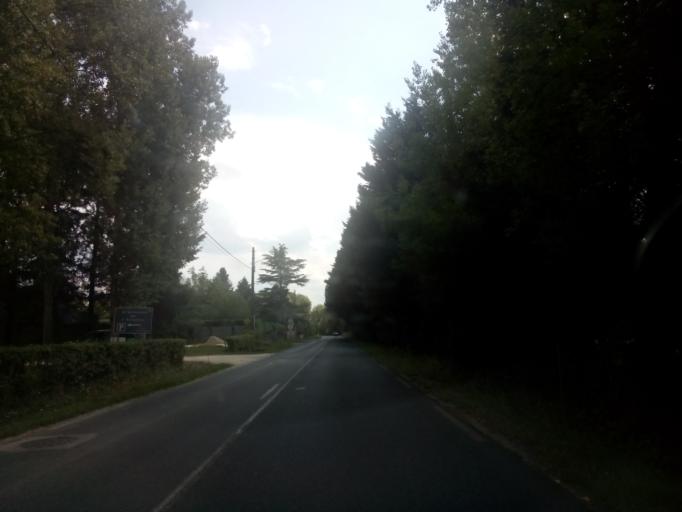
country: FR
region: Centre
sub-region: Departement d'Indre-et-Loire
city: Cheille
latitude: 47.2681
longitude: 0.4361
